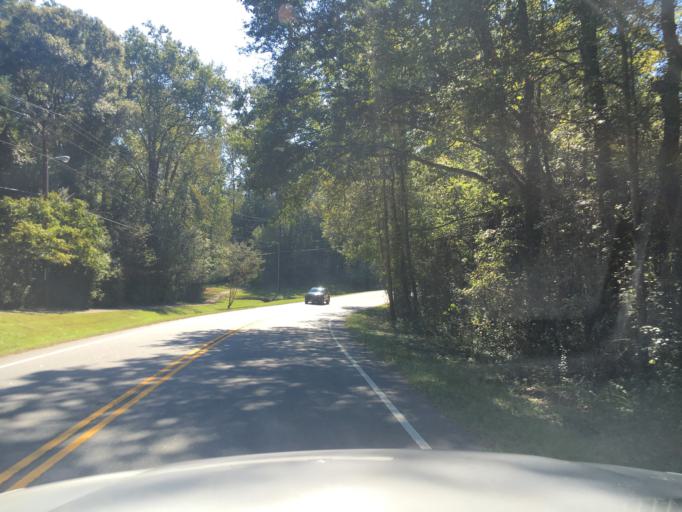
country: US
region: South Carolina
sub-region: Greenville County
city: Taylors
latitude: 34.8848
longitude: -82.2842
